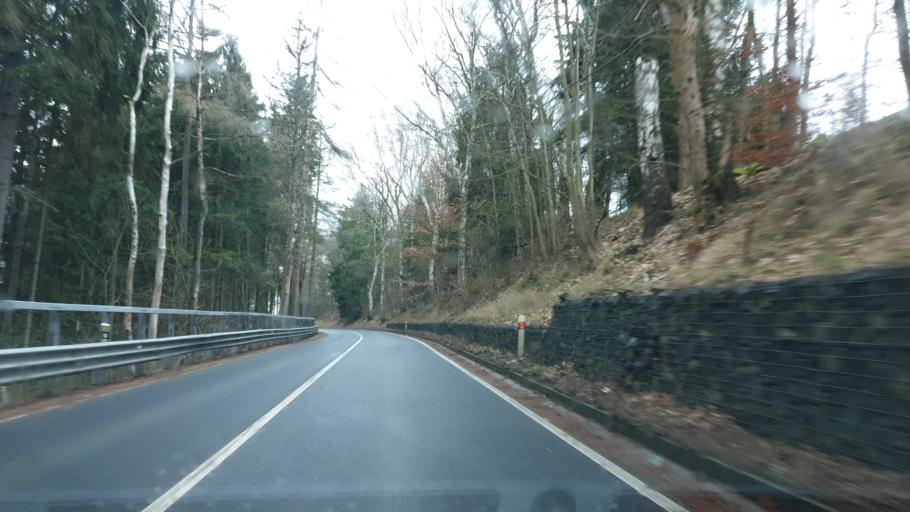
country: CZ
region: Karlovarsky
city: As
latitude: 50.2423
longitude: 12.1839
